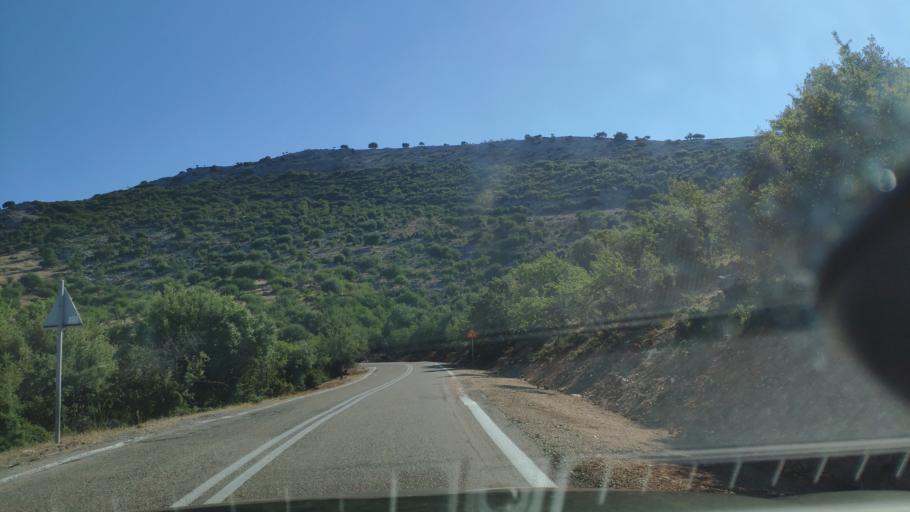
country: GR
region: West Greece
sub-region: Nomos Aitolias kai Akarnanias
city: Archontochorion
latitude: 38.6902
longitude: 21.0599
